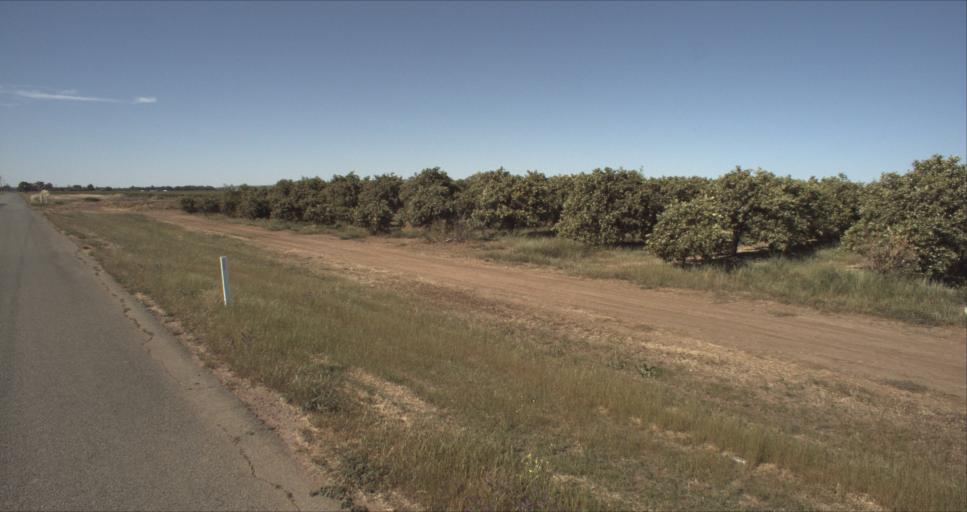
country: AU
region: New South Wales
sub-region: Leeton
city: Leeton
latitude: -34.5853
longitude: 146.3790
